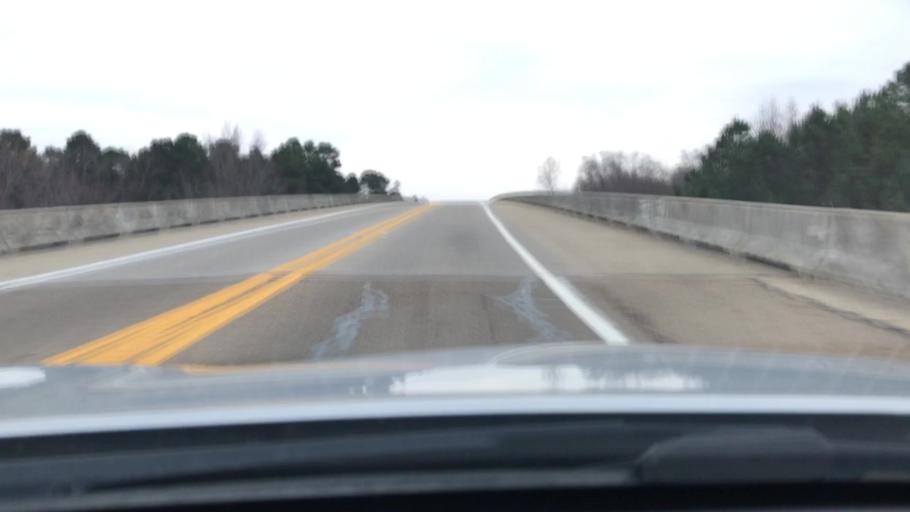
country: US
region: Arkansas
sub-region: Hempstead County
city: Hope
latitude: 33.6751
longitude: -93.5757
